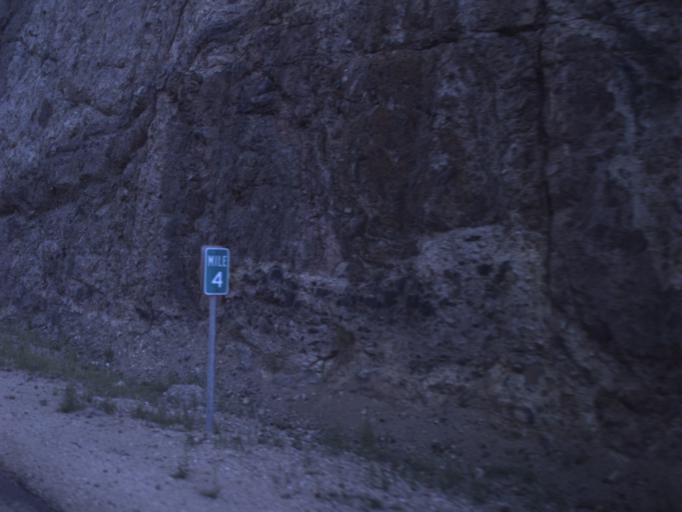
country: US
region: Utah
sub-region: Wasatch County
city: Heber
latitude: 40.5921
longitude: -111.3929
